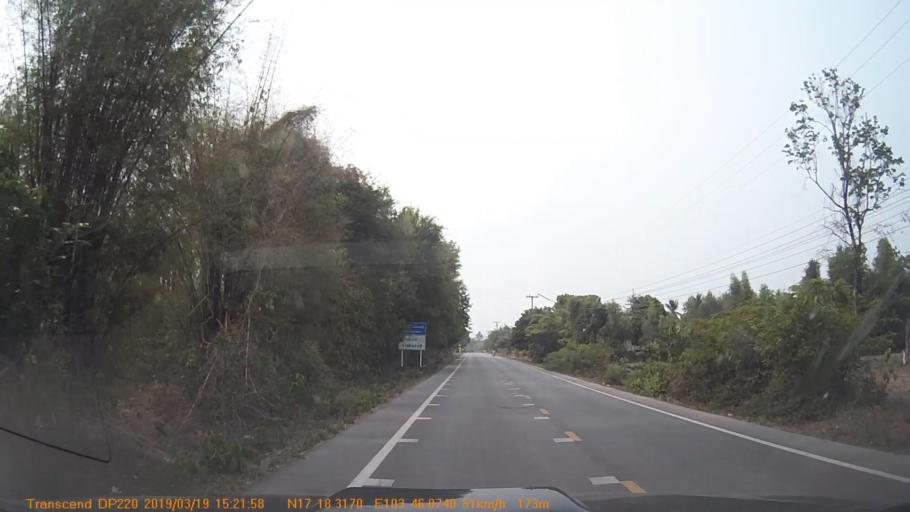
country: TH
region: Sakon Nakhon
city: Phanna Nikhom
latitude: 17.3054
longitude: 103.7678
